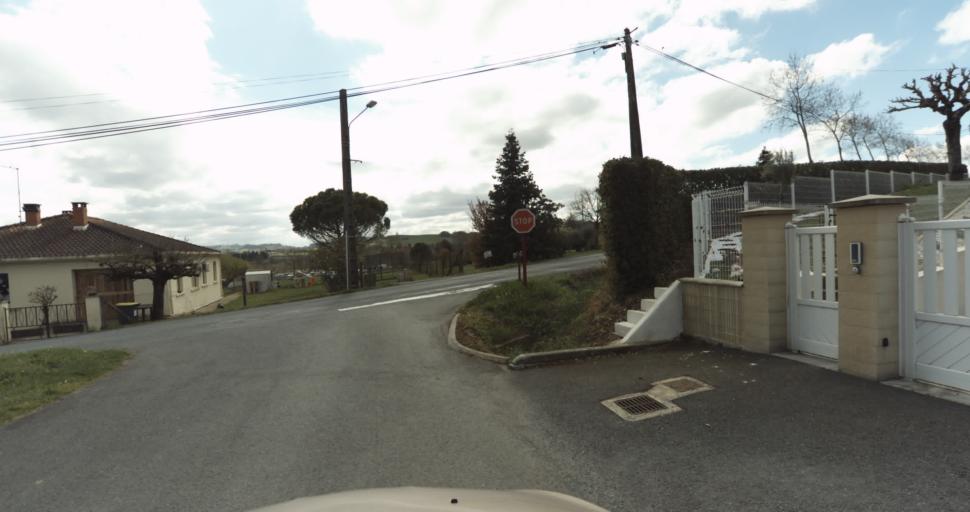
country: FR
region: Midi-Pyrenees
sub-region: Departement du Tarn
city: Puygouzon
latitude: 43.8943
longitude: 2.1484
